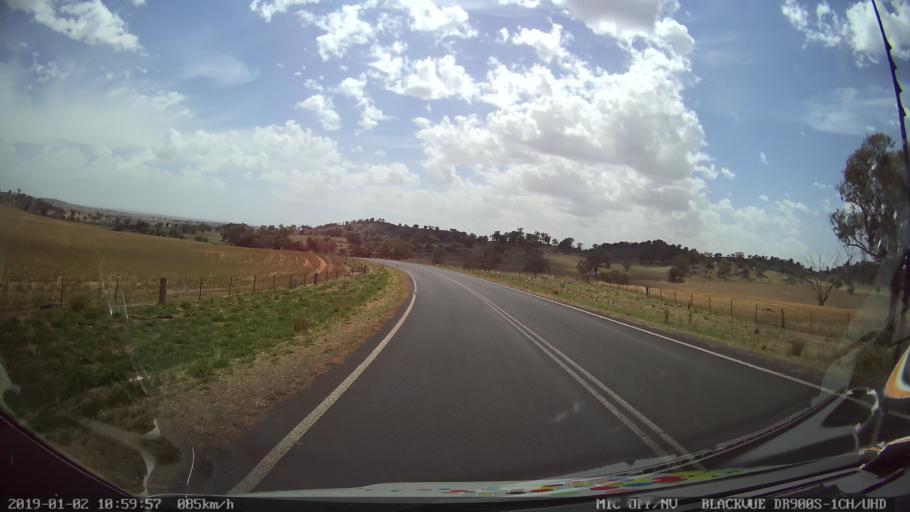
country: AU
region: New South Wales
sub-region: Cootamundra
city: Cootamundra
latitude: -34.6101
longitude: 148.3116
